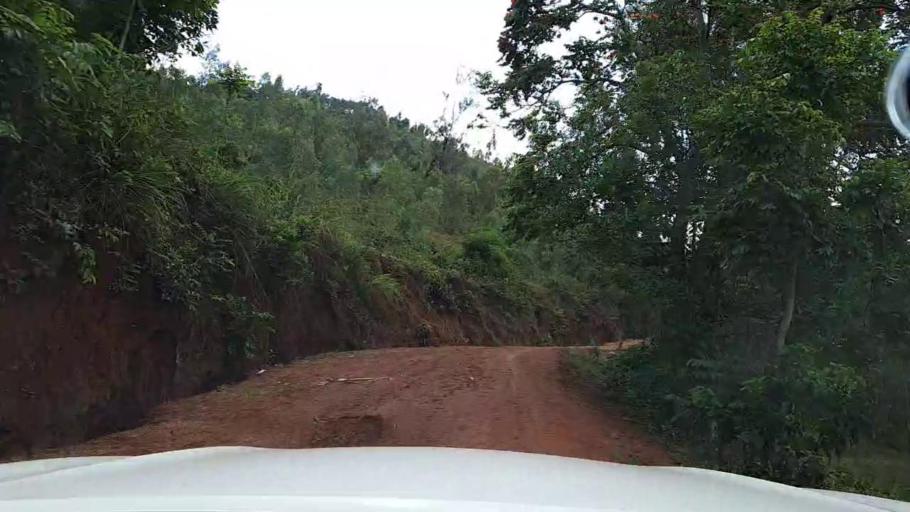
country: RW
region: Southern Province
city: Butare
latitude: -2.7458
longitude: 29.7641
